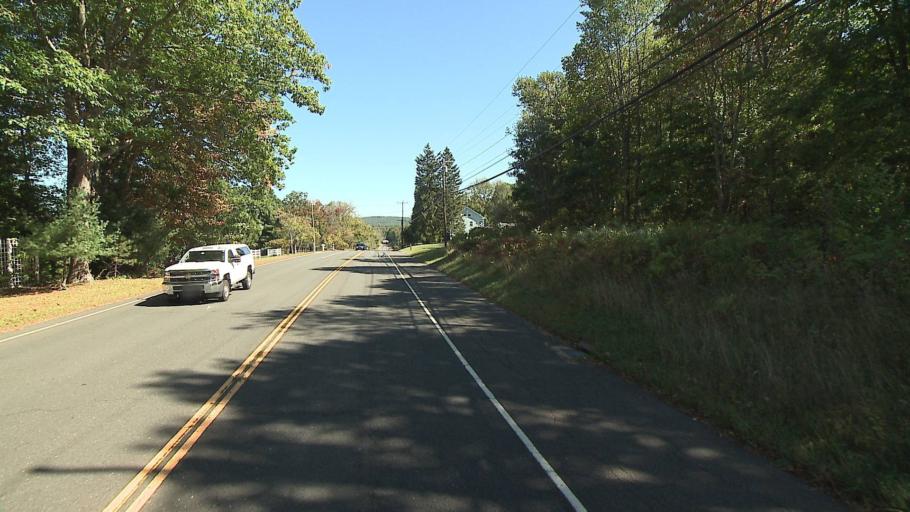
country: US
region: Connecticut
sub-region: Litchfield County
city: Northwest Harwinton
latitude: 41.8275
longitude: -73.0431
